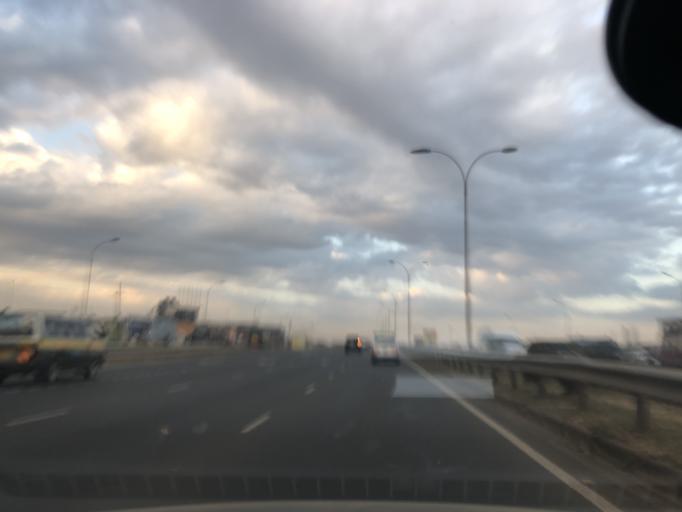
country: KE
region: Kiambu
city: Kiambu
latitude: -1.2064
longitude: 36.9145
